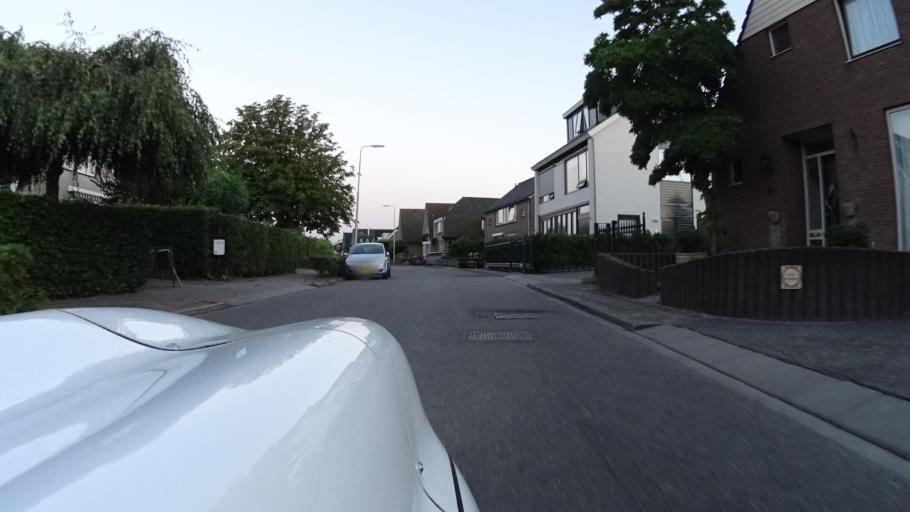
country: NL
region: South Holland
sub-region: Gemeente Kaag en Braassem
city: Oude Wetering
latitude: 52.1926
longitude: 4.6273
